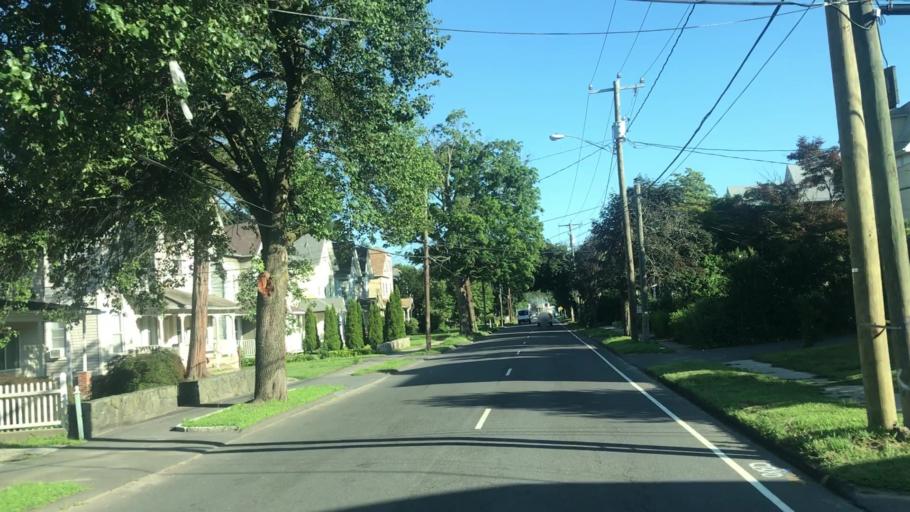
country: US
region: Connecticut
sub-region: Fairfield County
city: Danbury
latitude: 41.4014
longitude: -73.4538
